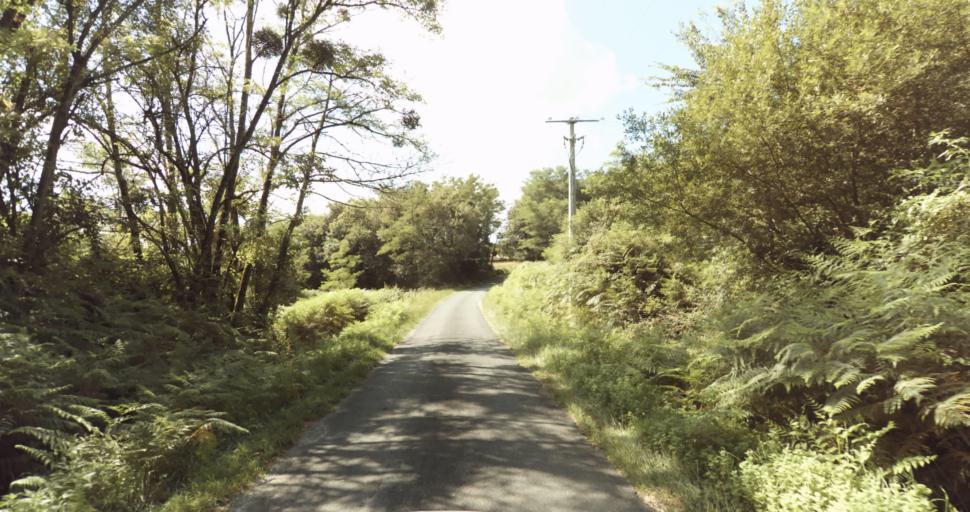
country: FR
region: Aquitaine
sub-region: Departement de la Gironde
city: Bazas
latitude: 44.4647
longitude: -0.2178
